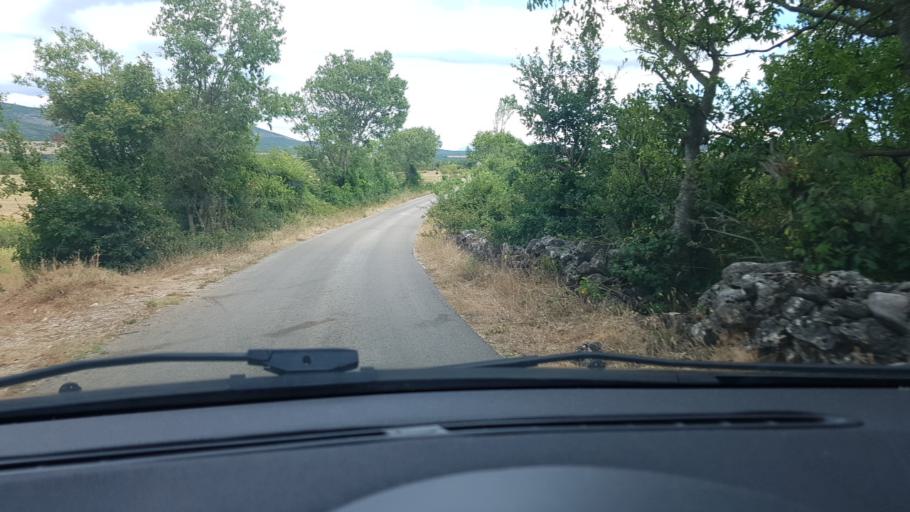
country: HR
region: Sibensko-Kniniska
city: Kistanje
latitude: 44.1097
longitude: 15.9267
